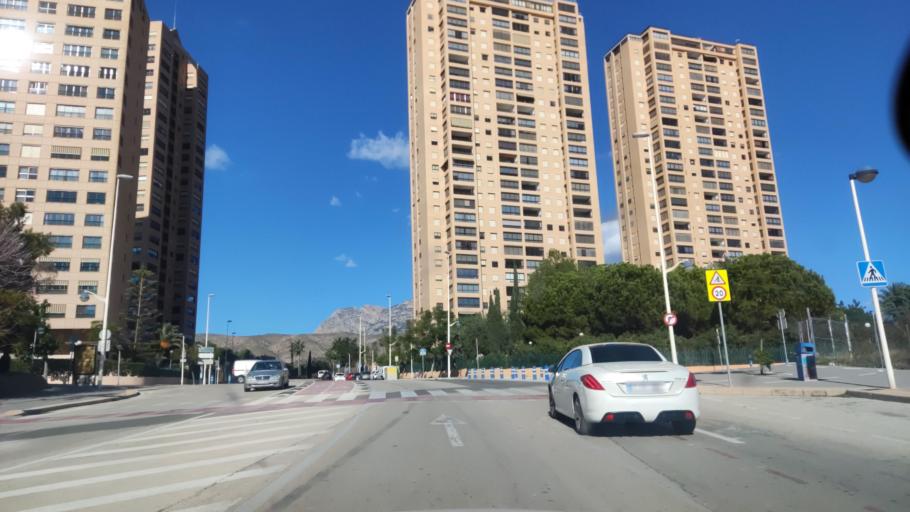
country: ES
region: Valencia
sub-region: Provincia de Alicante
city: Benidorm
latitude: 38.5361
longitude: -0.1570
